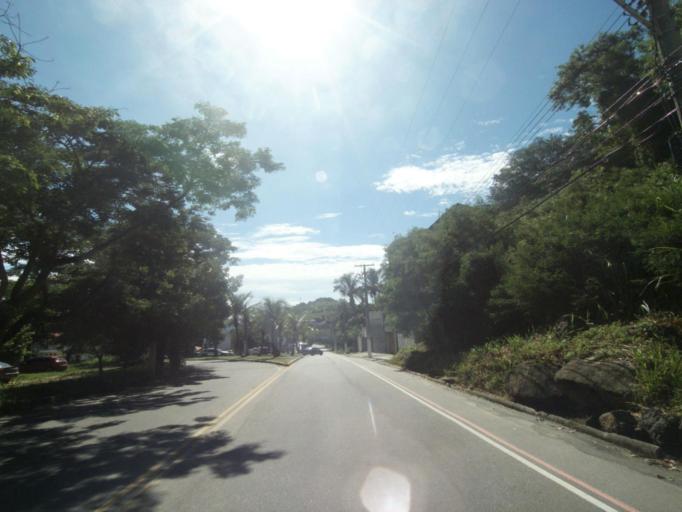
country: BR
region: Rio de Janeiro
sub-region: Niteroi
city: Niteroi
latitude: -22.9553
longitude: -43.0695
